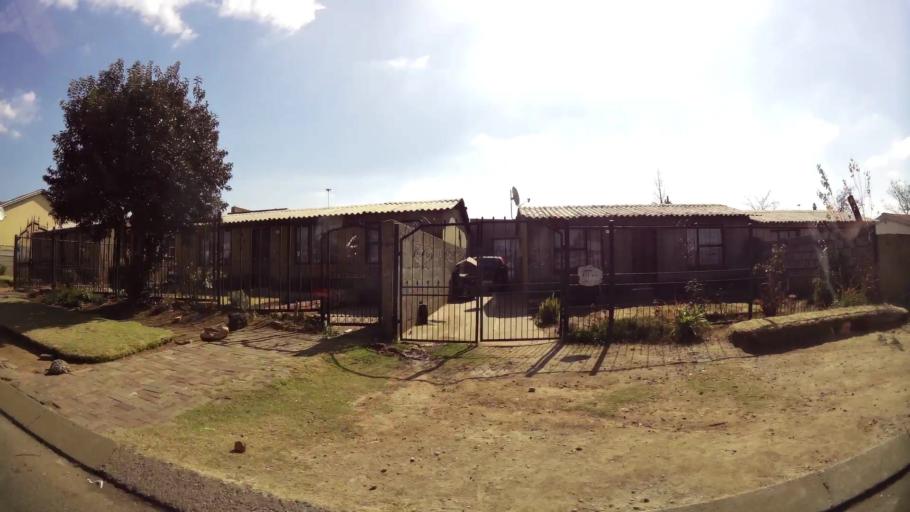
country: ZA
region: Gauteng
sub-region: City of Johannesburg Metropolitan Municipality
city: Soweto
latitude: -26.2494
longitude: 27.8861
